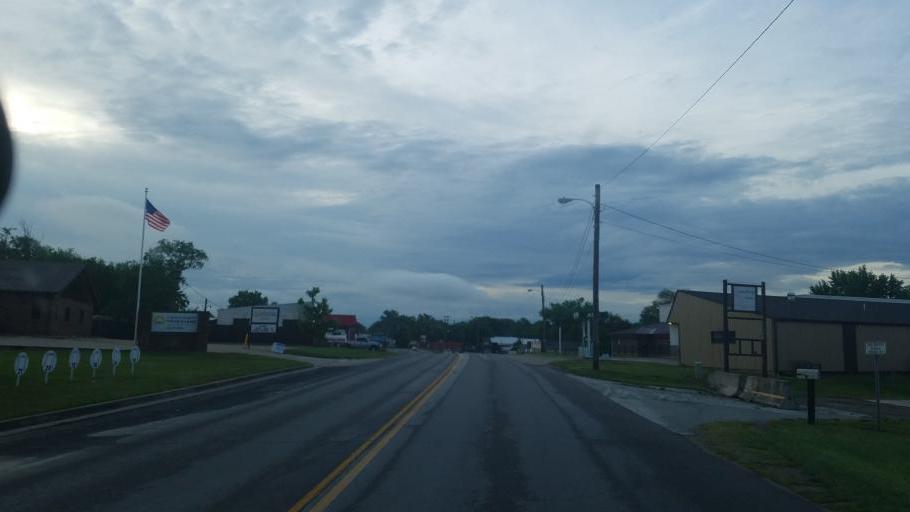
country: US
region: Missouri
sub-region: Moniteau County
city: California
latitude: 38.6285
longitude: -92.5763
